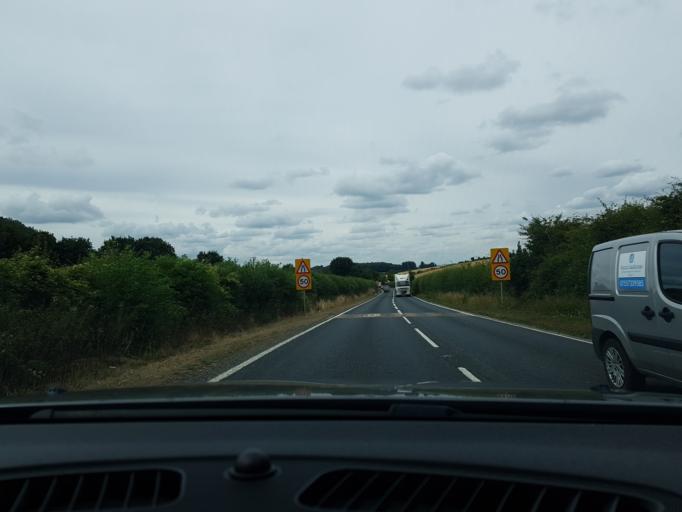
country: GB
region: England
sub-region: Hampshire
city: Tadley
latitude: 51.2922
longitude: -1.1677
